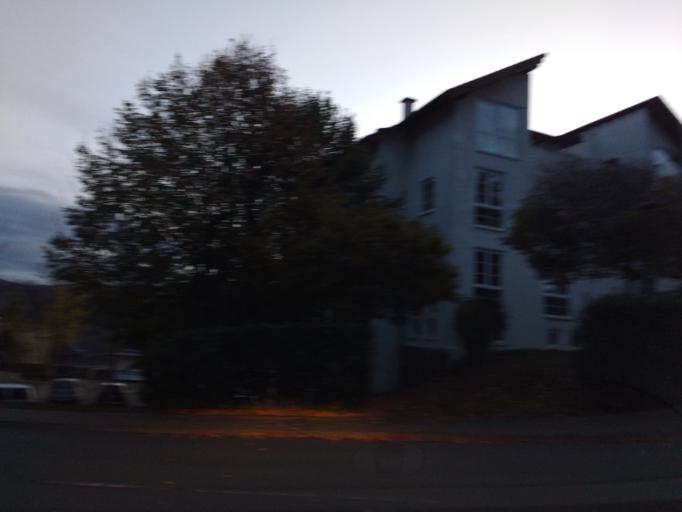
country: DE
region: Hesse
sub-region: Regierungsbezirk Kassel
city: Waldeck
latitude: 51.1872
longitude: 9.0595
